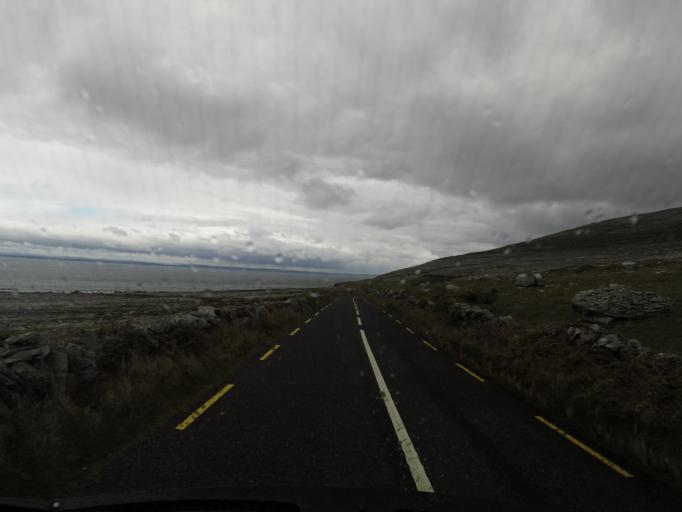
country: IE
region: Connaught
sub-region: County Galway
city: Bearna
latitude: 53.1432
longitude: -9.2742
